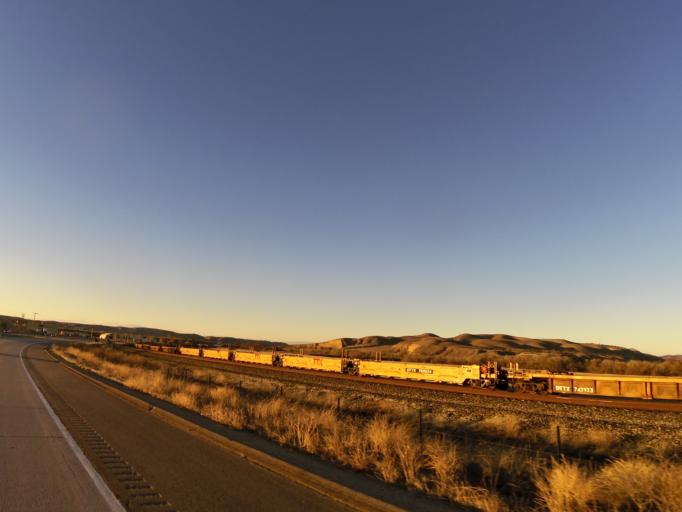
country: US
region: California
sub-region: San Luis Obispo County
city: San Miguel
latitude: 35.7807
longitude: -120.7220
